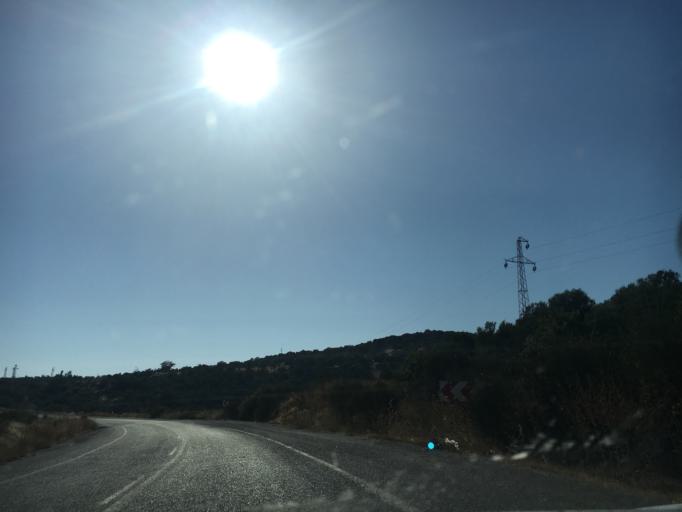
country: TR
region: Canakkale
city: Behram
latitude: 39.5067
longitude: 26.4073
